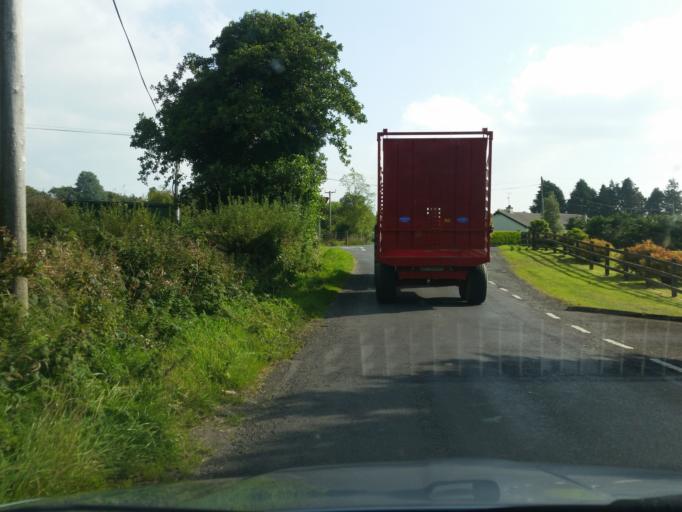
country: GB
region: Northern Ireland
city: Ballinamallard
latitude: 54.3368
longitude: -7.5364
